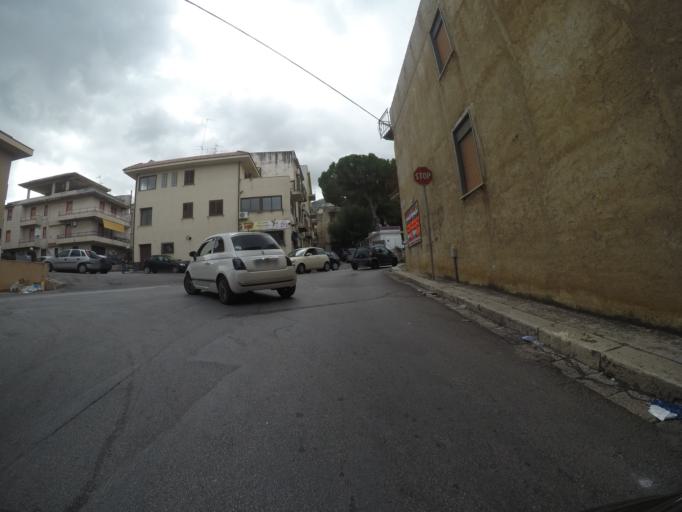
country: IT
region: Sicily
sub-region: Palermo
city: Carini
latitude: 38.1341
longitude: 13.1865
